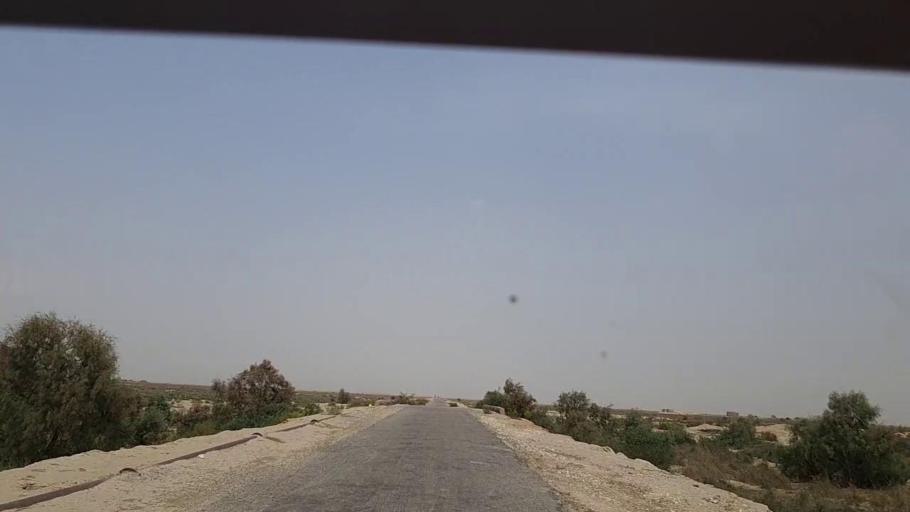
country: PK
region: Sindh
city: Phulji
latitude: 26.9999
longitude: 67.5183
